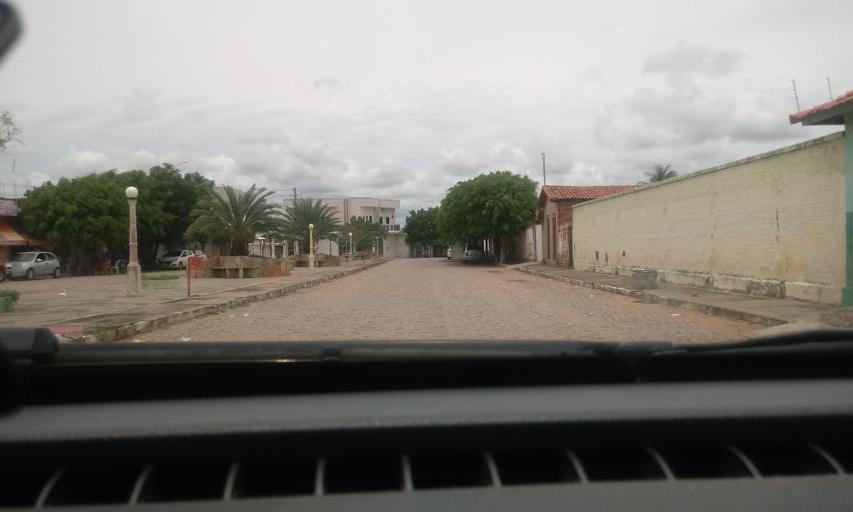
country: BR
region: Bahia
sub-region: Riacho De Santana
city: Riacho de Santana
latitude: -13.9104
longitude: -42.8478
